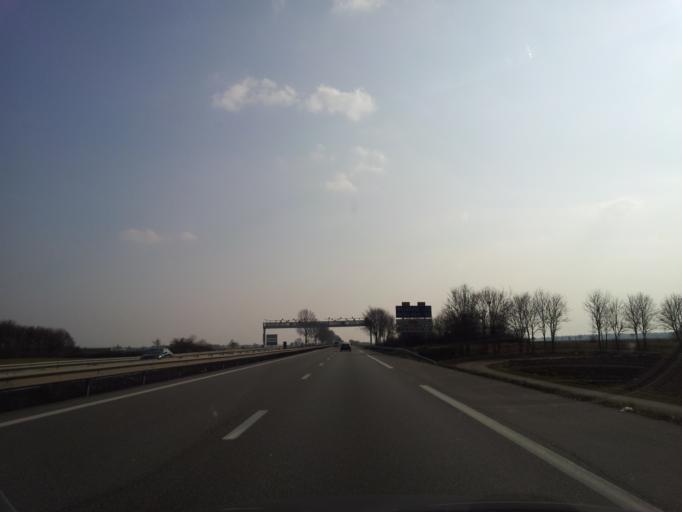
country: FR
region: Alsace
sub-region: Departement du Haut-Rhin
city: Oberhergheim
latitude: 47.9720
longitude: 7.3721
